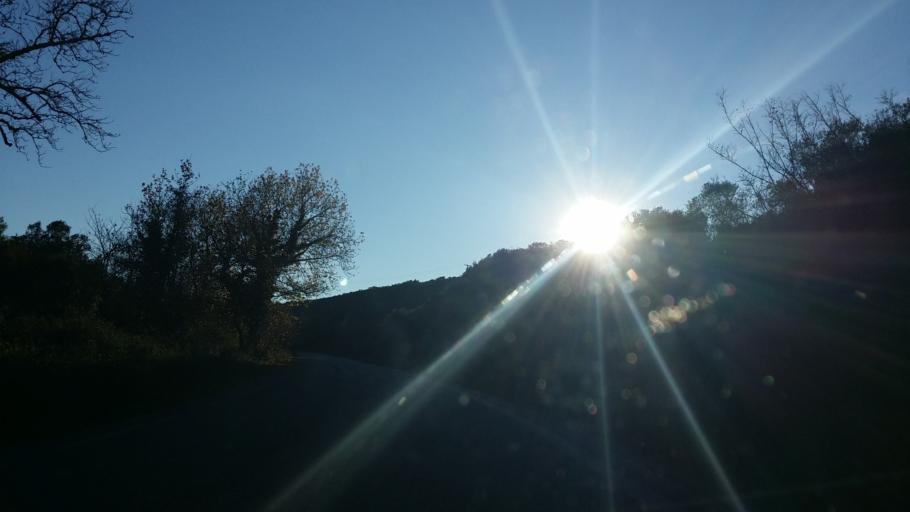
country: GR
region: West Greece
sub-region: Nomos Aitolias kai Akarnanias
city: Sardinia
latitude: 38.8489
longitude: 21.3336
